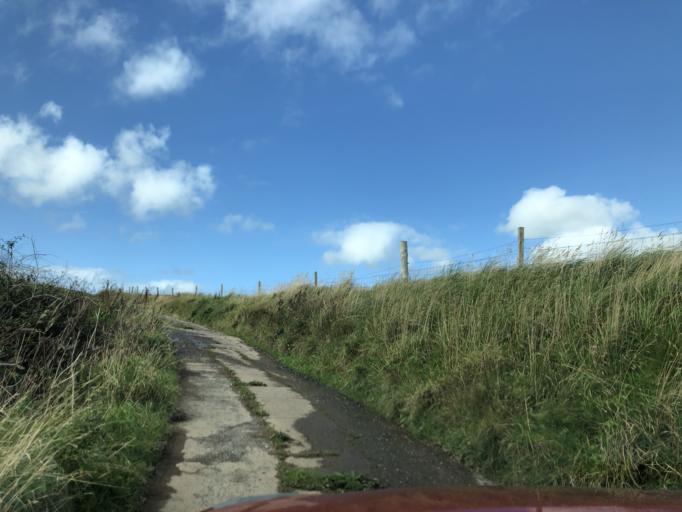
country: GB
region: Scotland
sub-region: Argyll and Bute
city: Campbeltown
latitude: 55.3088
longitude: -5.6071
